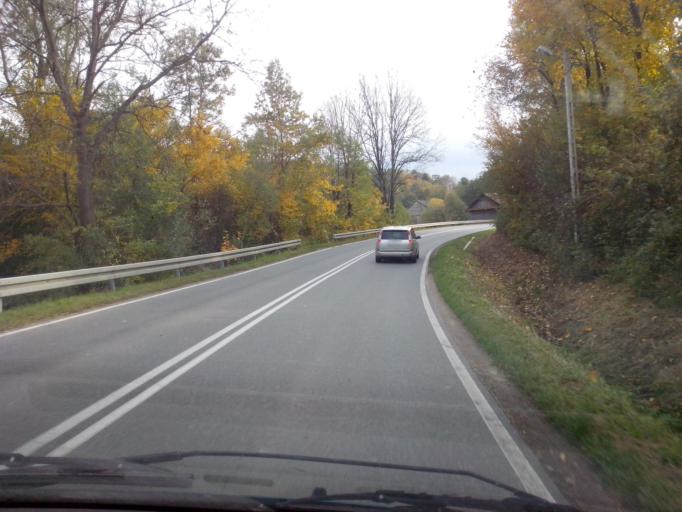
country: PL
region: Subcarpathian Voivodeship
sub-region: Powiat strzyzowski
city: Wisniowa
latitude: 49.8855
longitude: 21.6475
